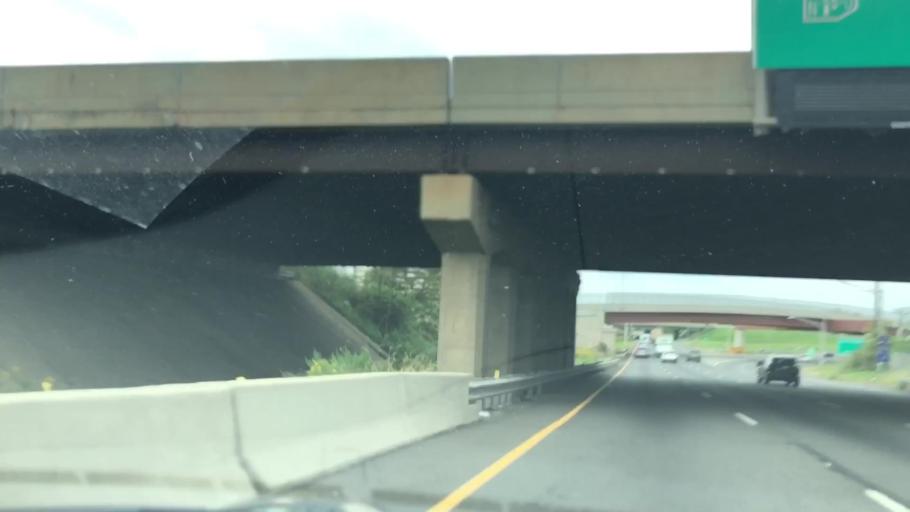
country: US
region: New Jersey
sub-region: Hudson County
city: Secaucus
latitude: 40.8034
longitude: -74.0709
